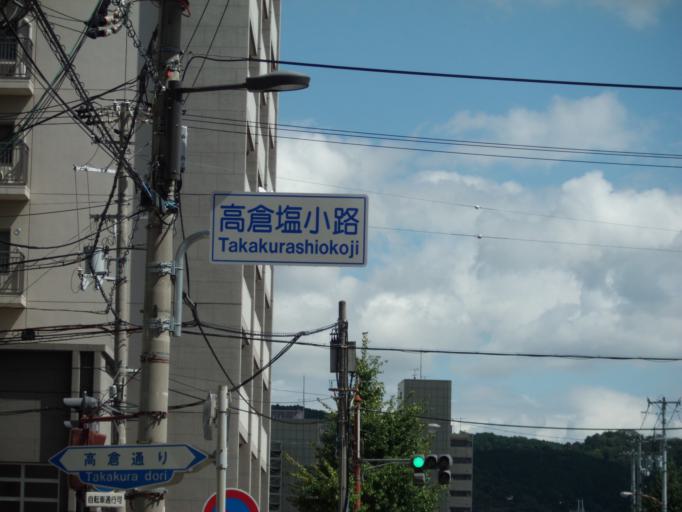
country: JP
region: Kyoto
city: Kyoto
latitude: 34.9873
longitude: 135.7619
